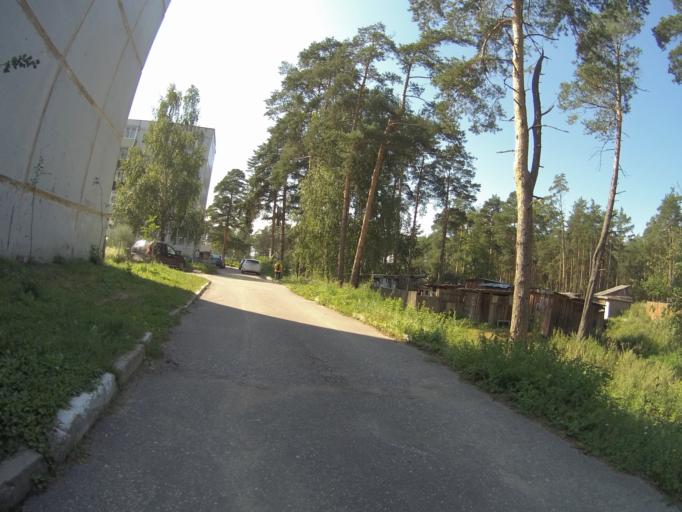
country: RU
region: Vladimir
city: Bogolyubovo
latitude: 56.2538
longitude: 40.5526
